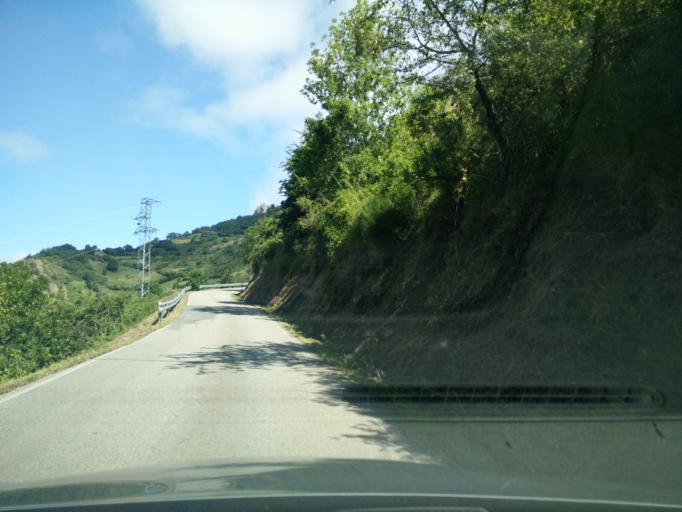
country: ES
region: Asturias
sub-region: Province of Asturias
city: Pola de Somiedo
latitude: 43.0853
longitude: -6.2359
